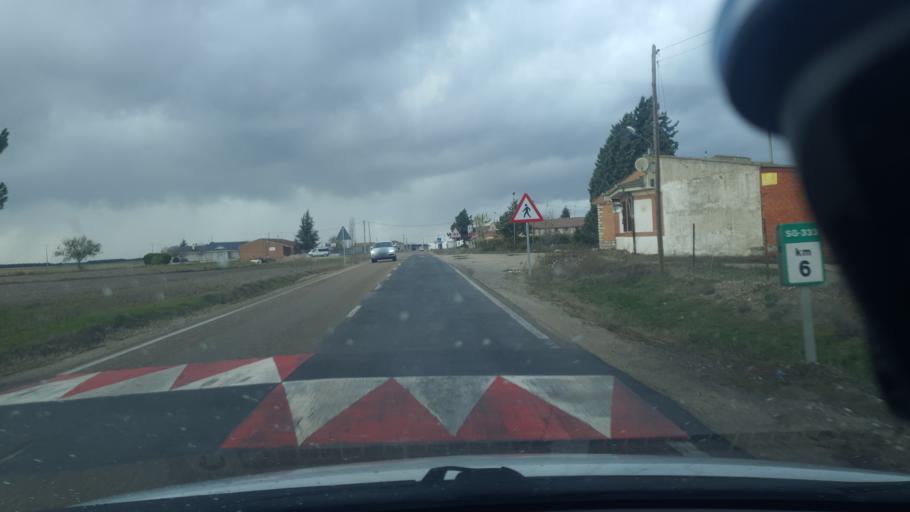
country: ES
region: Castille and Leon
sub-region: Provincia de Segovia
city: Sanchonuno
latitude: 41.3094
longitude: -4.3639
